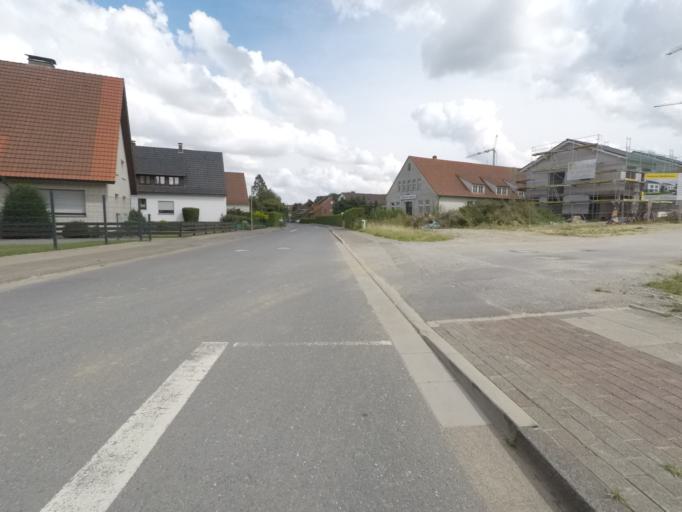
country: DE
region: North Rhine-Westphalia
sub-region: Regierungsbezirk Detmold
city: Bielefeld
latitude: 52.0444
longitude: 8.4731
